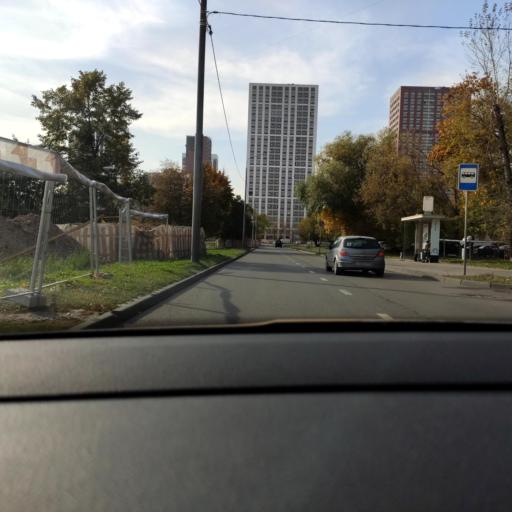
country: RU
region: Moscow
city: Metrogorodok
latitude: 55.8193
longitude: 37.7569
